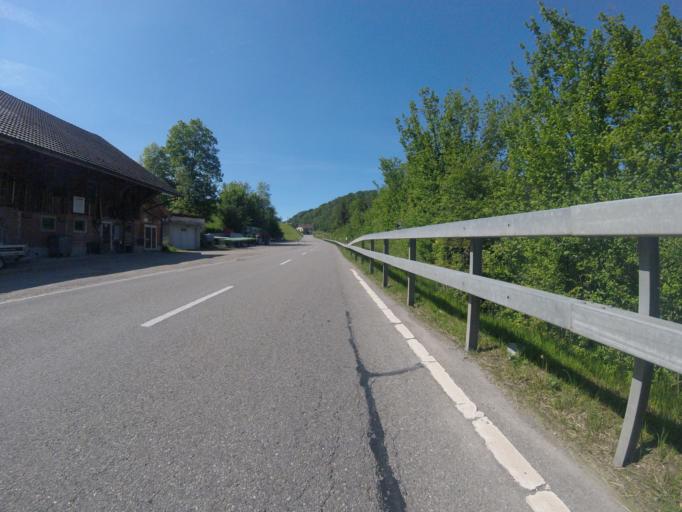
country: CH
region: Saint Gallen
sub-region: Wahlkreis Toggenburg
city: Ganterschwil
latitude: 47.3792
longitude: 9.1135
